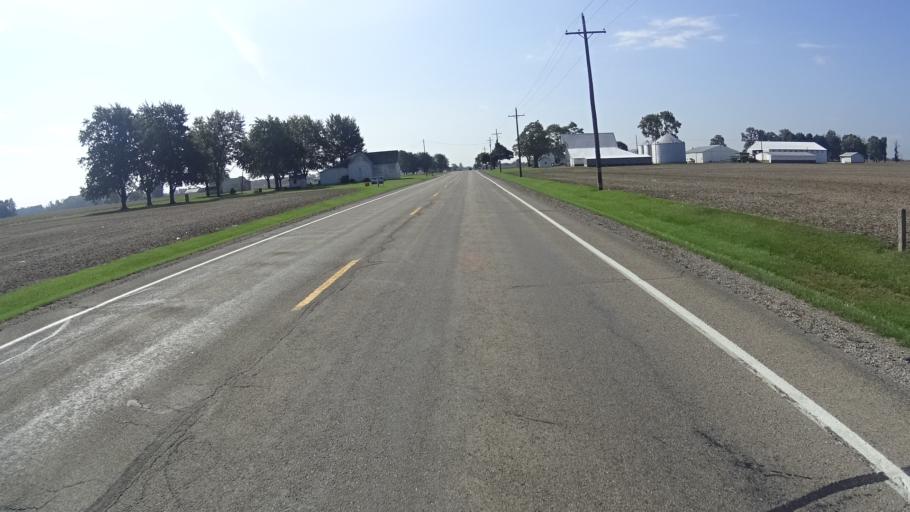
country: US
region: Indiana
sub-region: Madison County
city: Lapel
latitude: 40.0067
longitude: -85.8432
